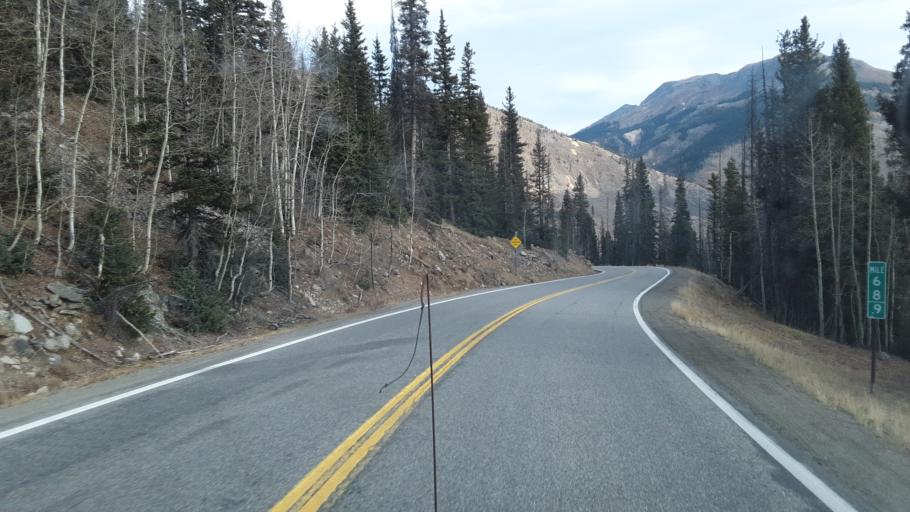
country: US
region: Colorado
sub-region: San Juan County
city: Silverton
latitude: 37.7965
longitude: -107.6742
